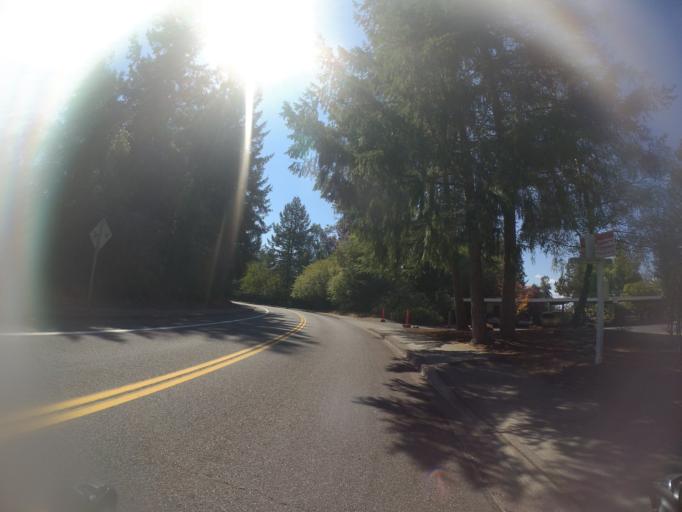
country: US
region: Washington
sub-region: Pierce County
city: University Place
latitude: 47.2161
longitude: -122.5649
